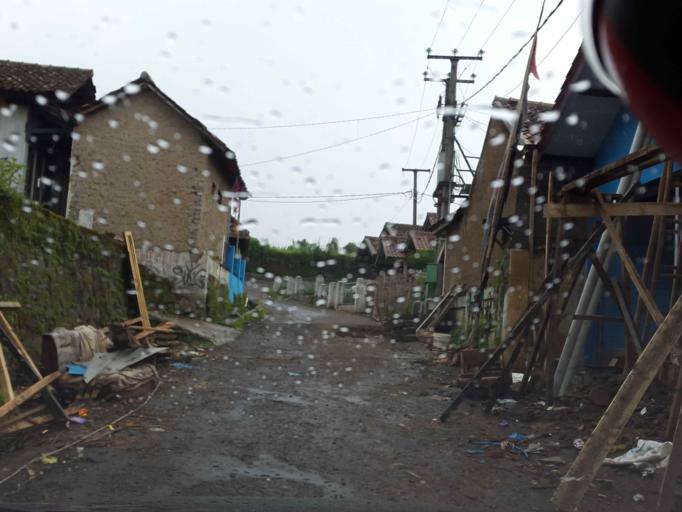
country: ID
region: West Java
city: Padalarang
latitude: -6.8306
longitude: 107.5073
